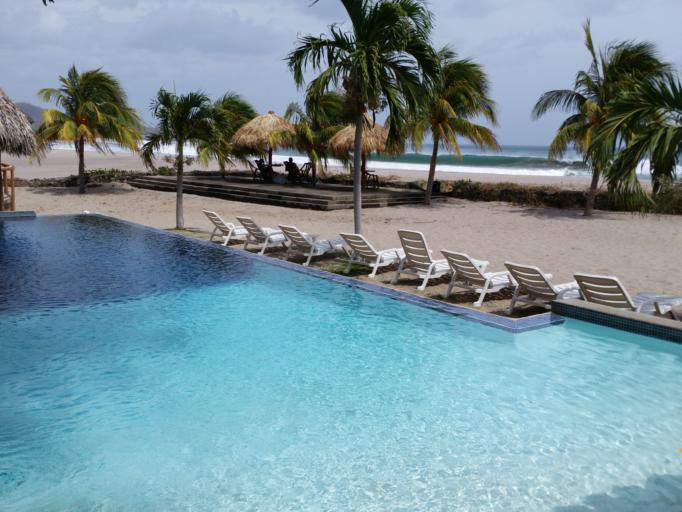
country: NI
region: Rivas
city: Tola
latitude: 11.4069
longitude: -86.0480
